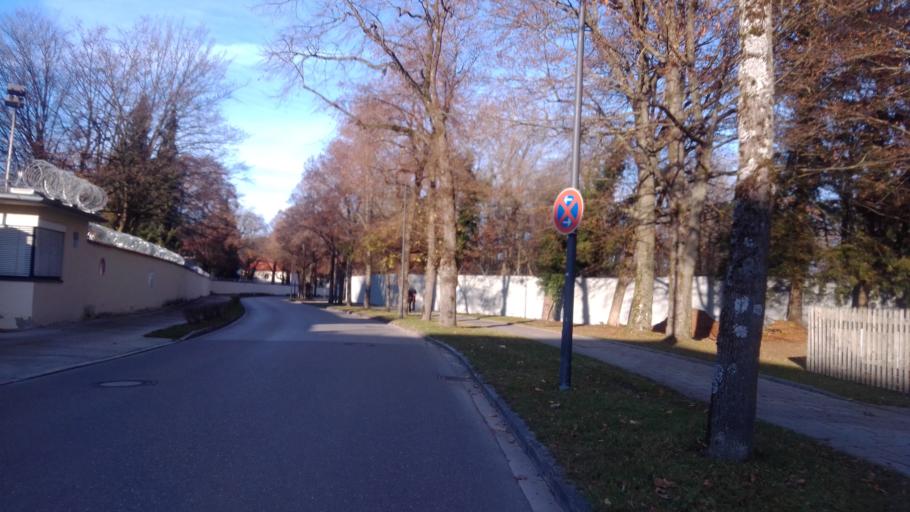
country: DE
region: Bavaria
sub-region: Upper Bavaria
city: Pullach im Isartal
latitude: 48.0611
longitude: 11.5277
